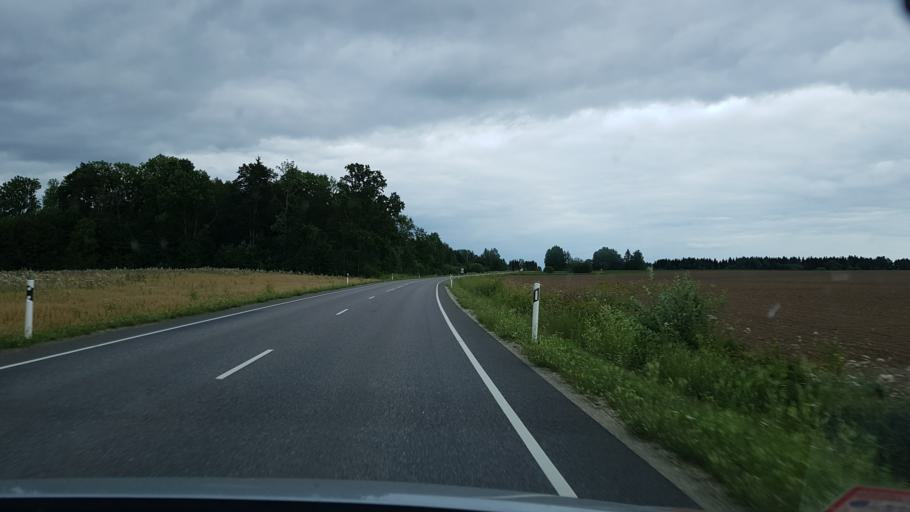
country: EE
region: Tartu
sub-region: Tartu linn
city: Tartu
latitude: 58.4134
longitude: 26.8877
